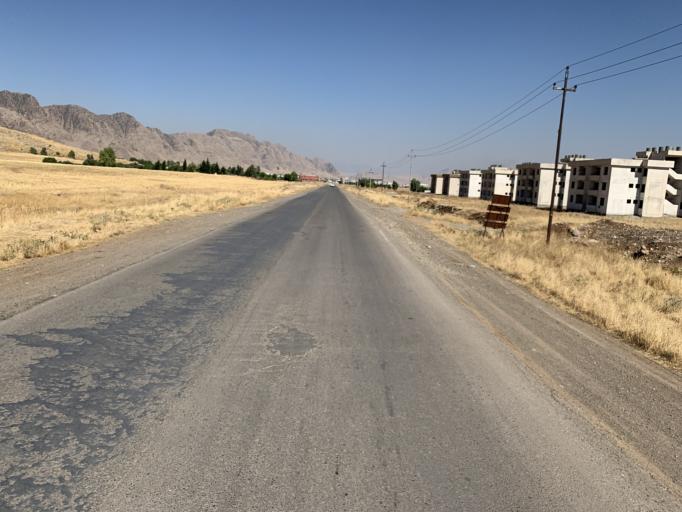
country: IQ
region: As Sulaymaniyah
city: Raniye
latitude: 36.2650
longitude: 44.8434
